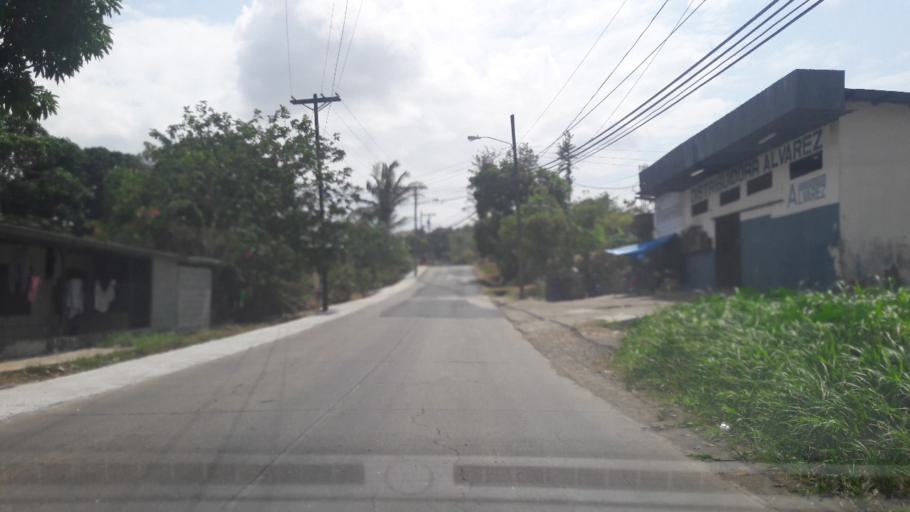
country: PA
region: Panama
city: Alcalde Diaz
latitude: 9.1380
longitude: -79.5526
